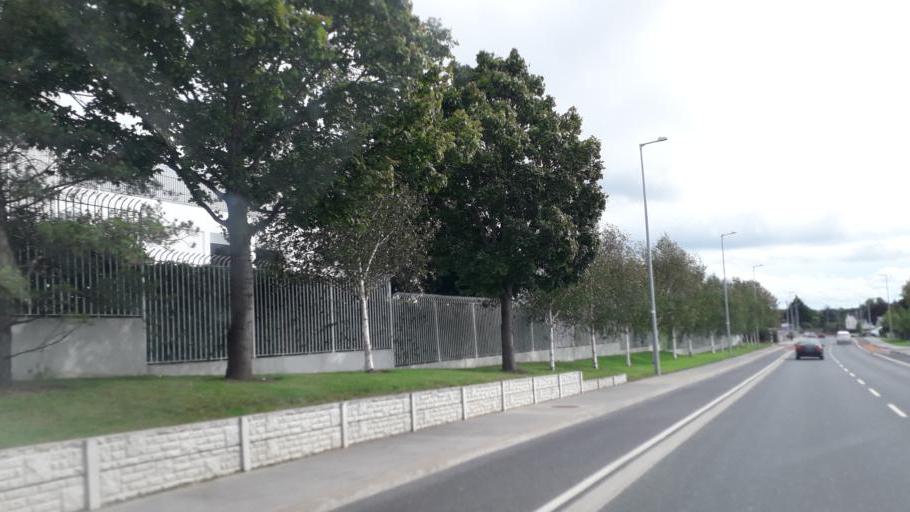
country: IE
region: Leinster
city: Cabinteely
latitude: 53.2707
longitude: -6.1513
